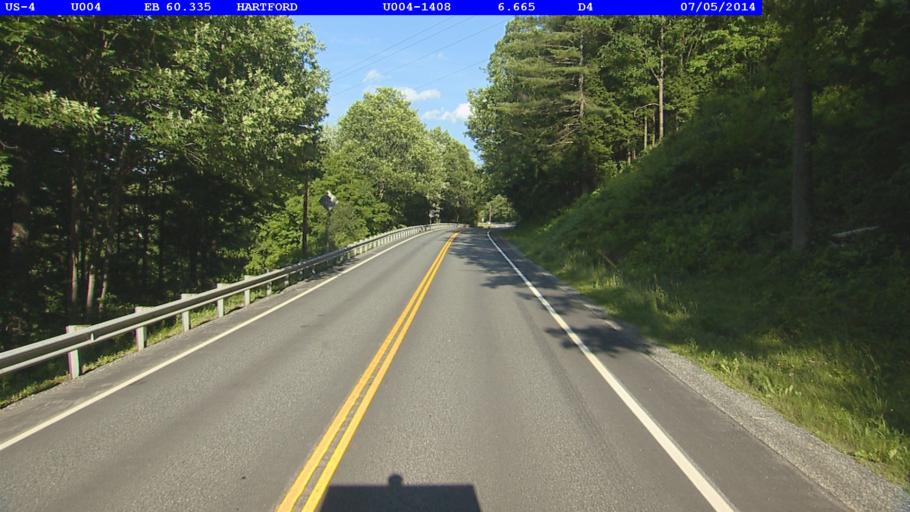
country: US
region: Vermont
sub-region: Windsor County
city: White River Junction
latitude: 43.6648
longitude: -72.3786
